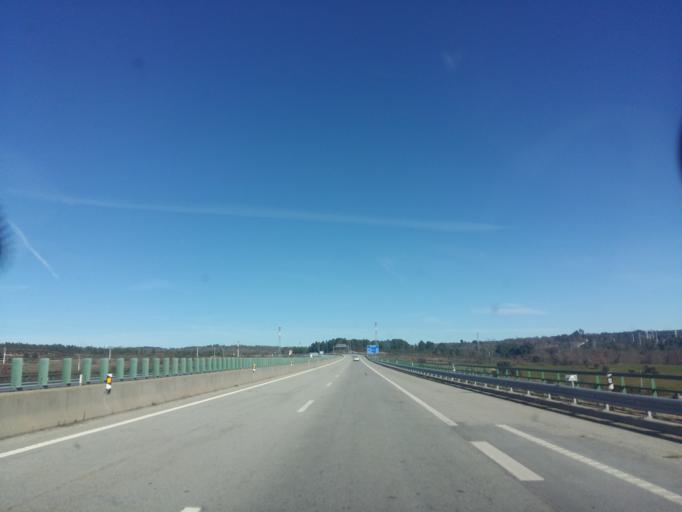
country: PT
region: Guarda
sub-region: Guarda
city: Sequeira
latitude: 40.5272
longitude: -7.2220
